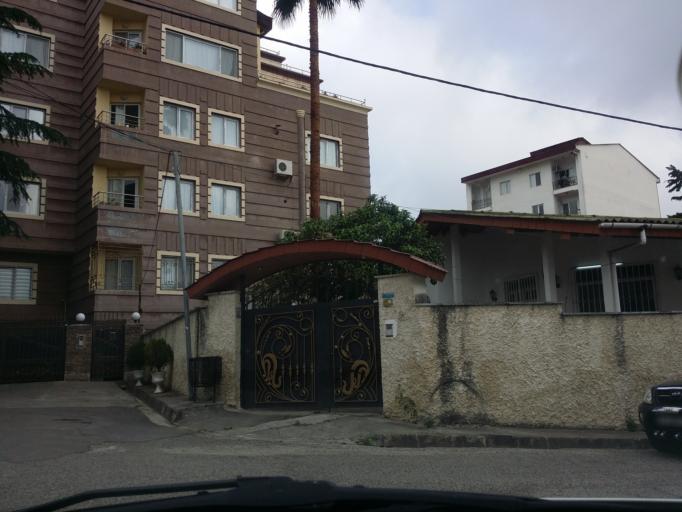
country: IR
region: Mazandaran
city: Chalus
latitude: 36.6487
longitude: 51.4193
